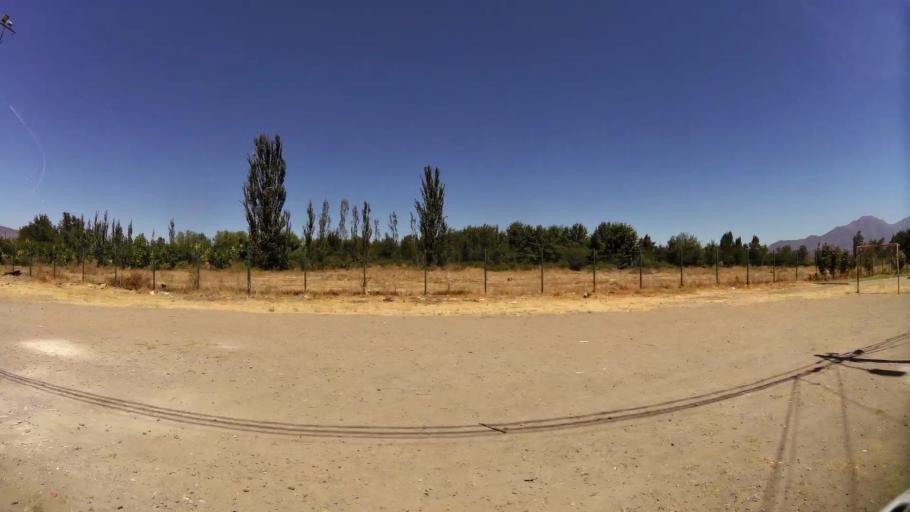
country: CL
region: O'Higgins
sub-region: Provincia de Cachapoal
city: Rancagua
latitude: -34.1581
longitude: -70.7557
